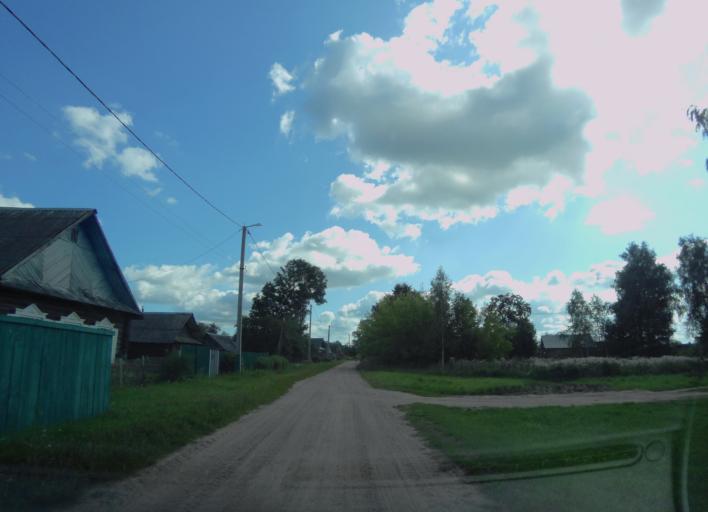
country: BY
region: Minsk
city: Zyembin
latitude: 54.3777
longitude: 28.3673
